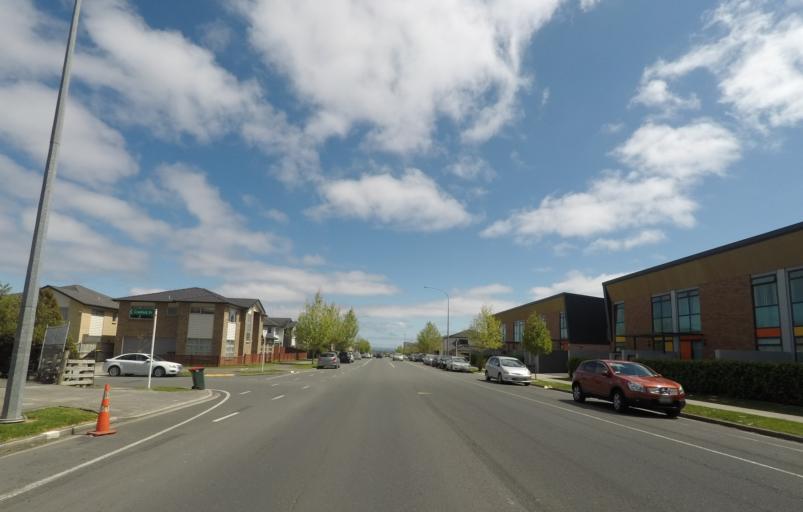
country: NZ
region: Auckland
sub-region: Auckland
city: Manukau City
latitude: -36.9749
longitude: 174.9216
